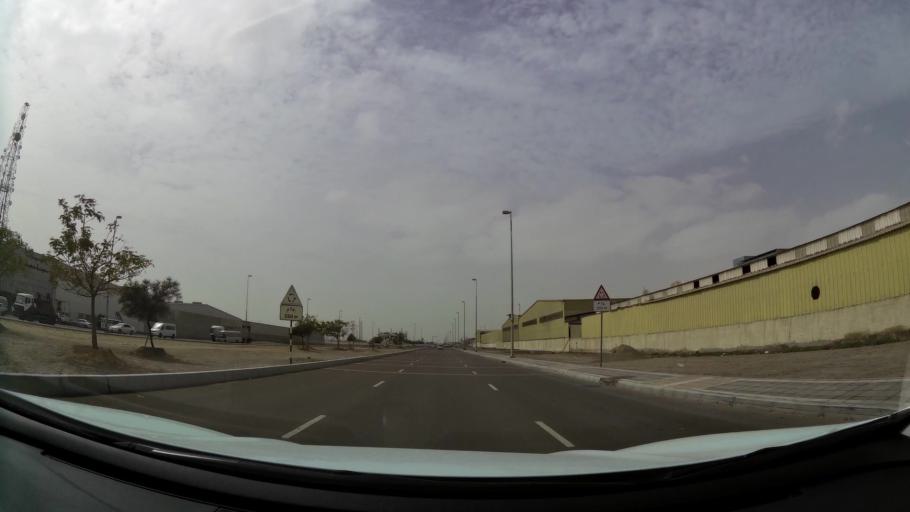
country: AE
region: Abu Dhabi
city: Abu Dhabi
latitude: 24.3679
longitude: 54.4847
